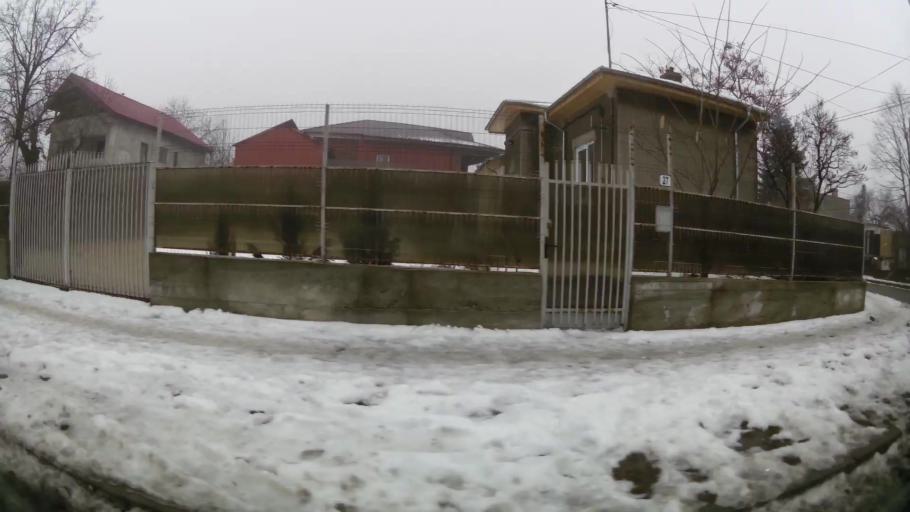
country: RO
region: Ilfov
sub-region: Comuna Chiajna
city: Rosu
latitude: 44.4747
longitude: 26.0053
